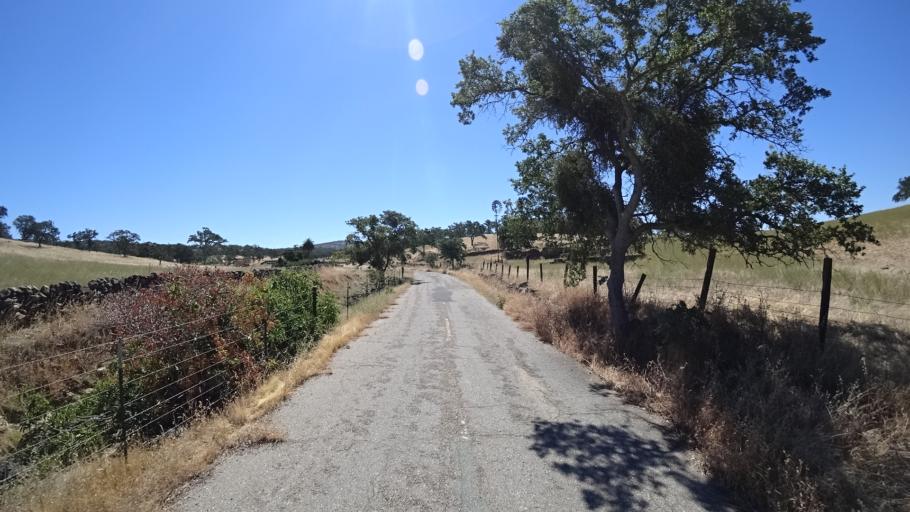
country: US
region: California
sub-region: Calaveras County
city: Copperopolis
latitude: 37.9358
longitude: -120.7444
